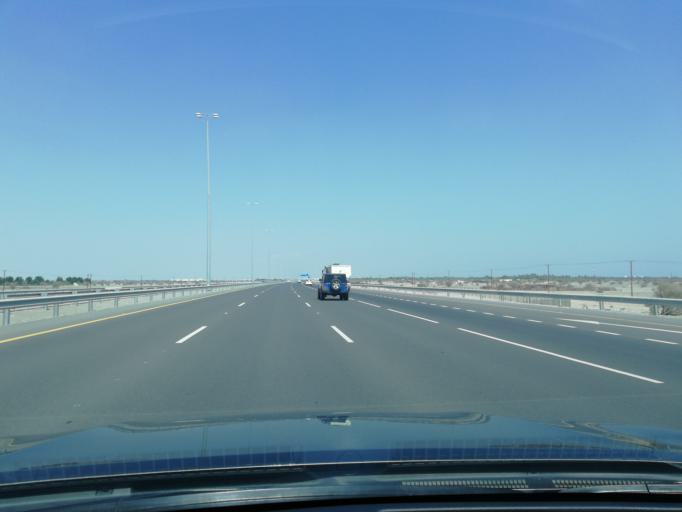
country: OM
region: Al Batinah
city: Barka'
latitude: 23.6218
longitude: 57.9006
